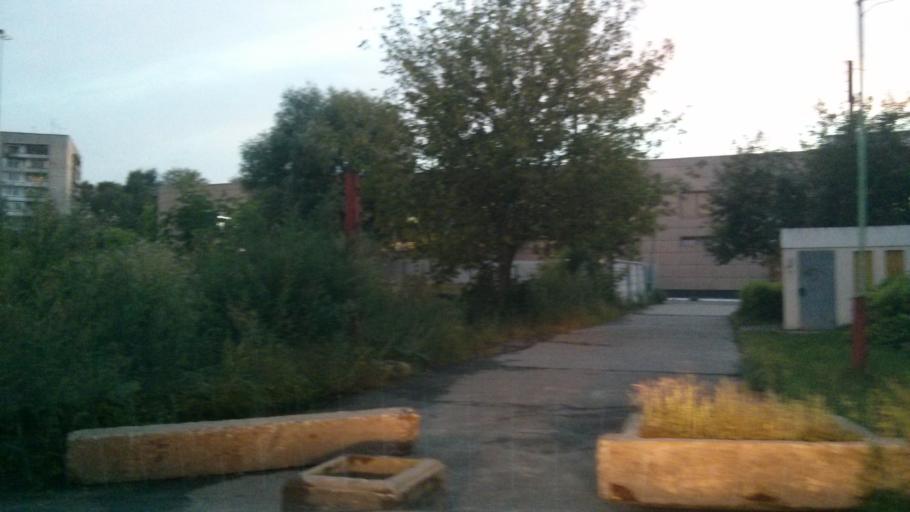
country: RU
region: Nizjnij Novgorod
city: Nizhniy Novgorod
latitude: 56.2964
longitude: 44.0397
